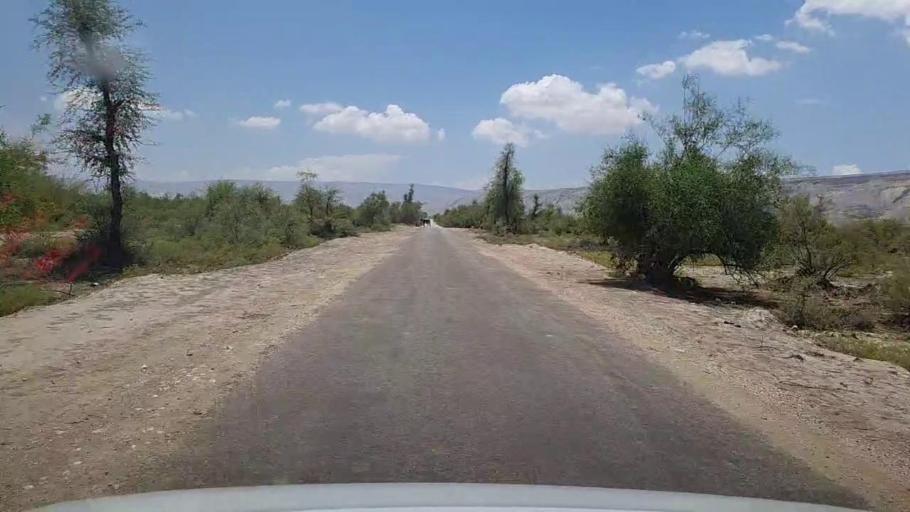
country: PK
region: Sindh
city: Bhan
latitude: 26.2799
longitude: 67.5289
